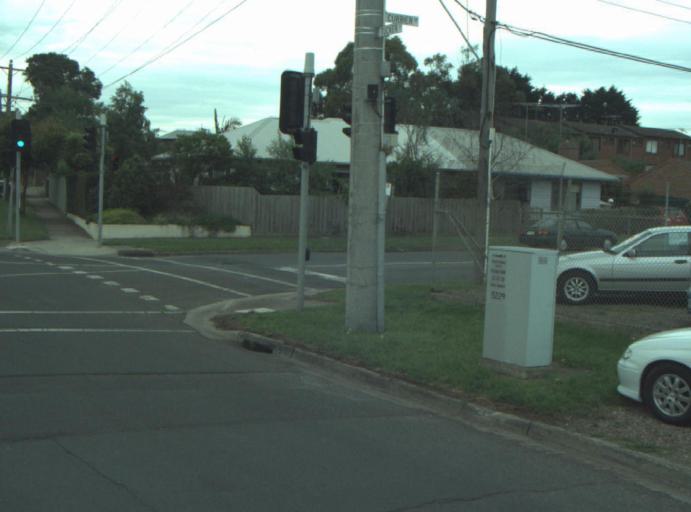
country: AU
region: Victoria
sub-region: Greater Geelong
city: Breakwater
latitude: -38.1826
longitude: 144.3666
